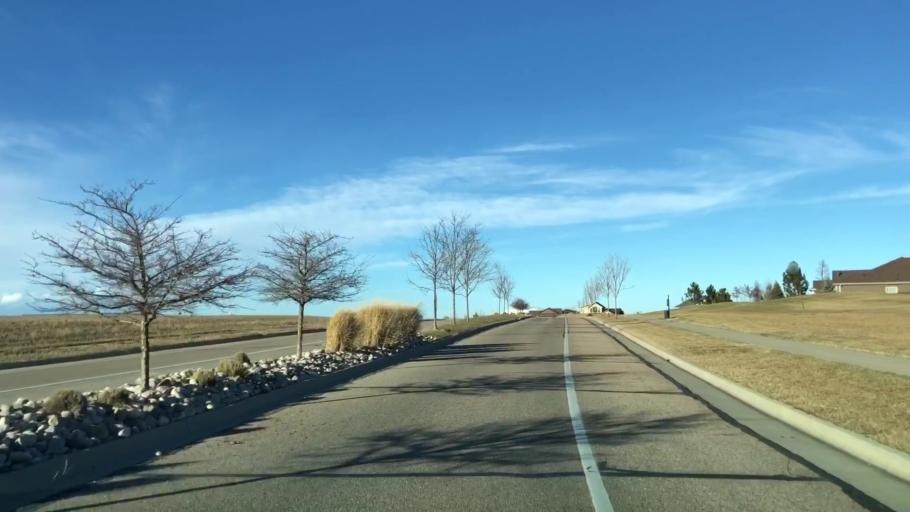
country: US
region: Colorado
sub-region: Weld County
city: Windsor
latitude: 40.4513
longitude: -104.9769
